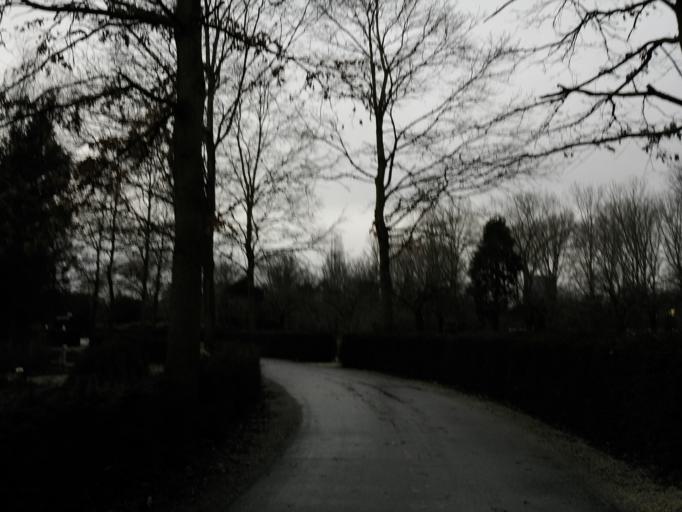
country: NL
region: North Holland
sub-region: Gemeente Amsterdam
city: Amsterdam
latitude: 52.3366
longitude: 4.8987
